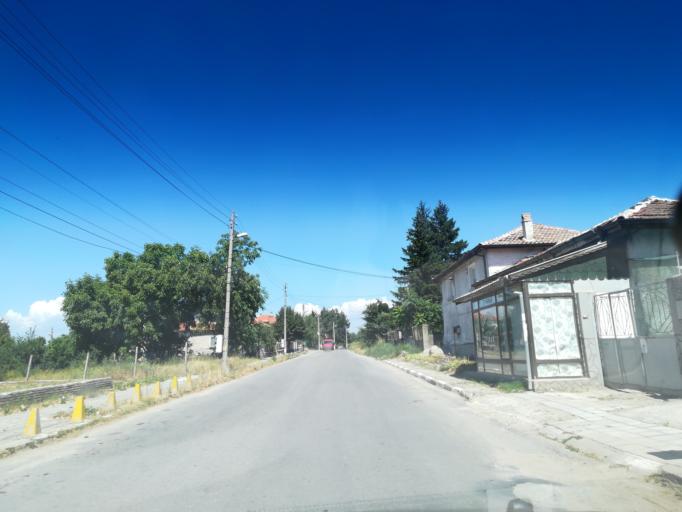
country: BG
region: Plovdiv
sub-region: Obshtina Asenovgrad
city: Asenovgrad
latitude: 42.0206
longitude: 24.9708
